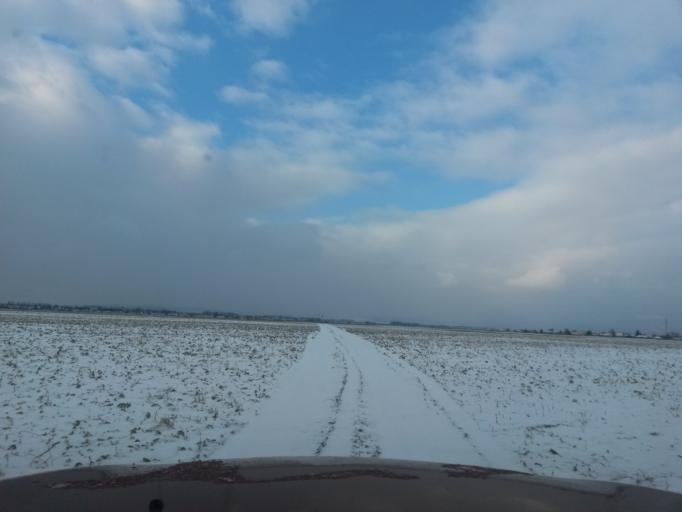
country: SK
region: Kosicky
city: Kosice
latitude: 48.6339
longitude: 21.3365
